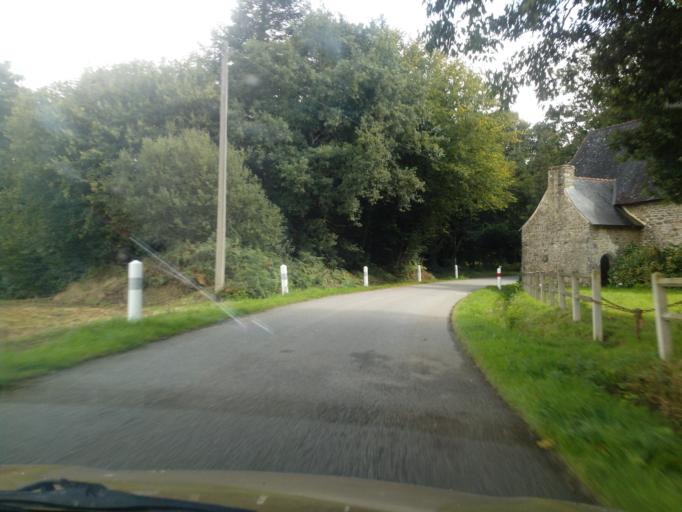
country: FR
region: Brittany
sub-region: Departement des Cotes-d'Armor
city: Merdrignac
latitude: 48.1334
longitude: -2.3929
